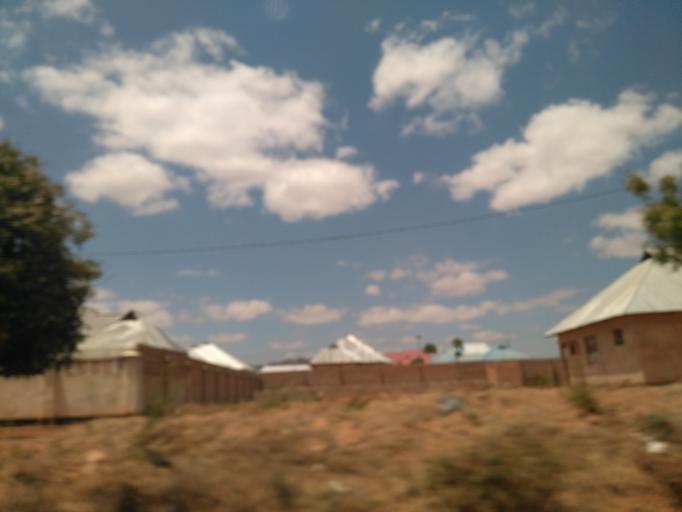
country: TZ
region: Dodoma
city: Kisasa
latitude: -6.1764
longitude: 35.7924
